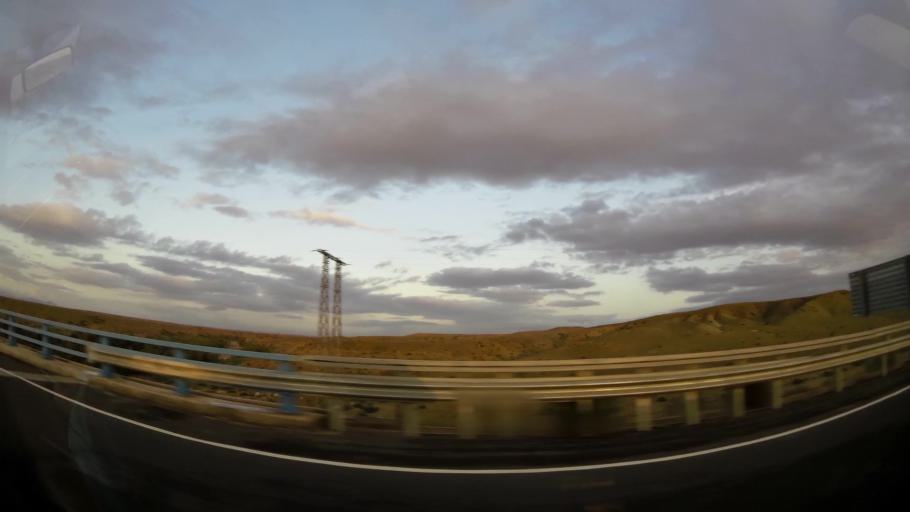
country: MA
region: Oriental
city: Taourirt
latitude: 34.5358
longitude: -2.9161
